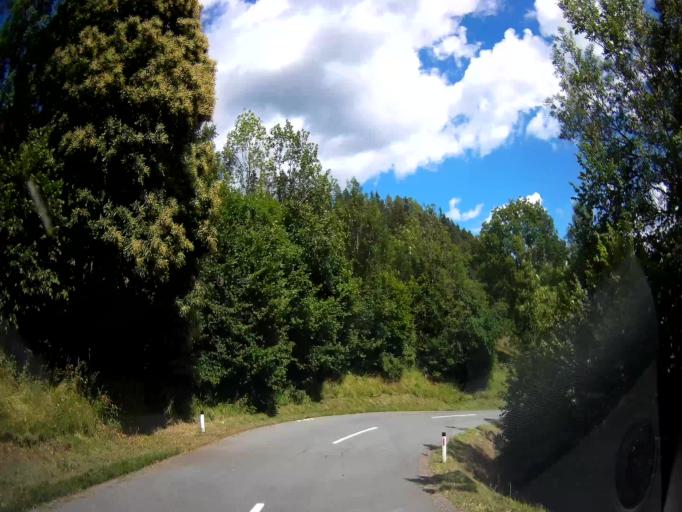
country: AT
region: Carinthia
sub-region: Politischer Bezirk Sankt Veit an der Glan
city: St. Georgen am Laengsee
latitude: 46.7228
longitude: 14.4331
